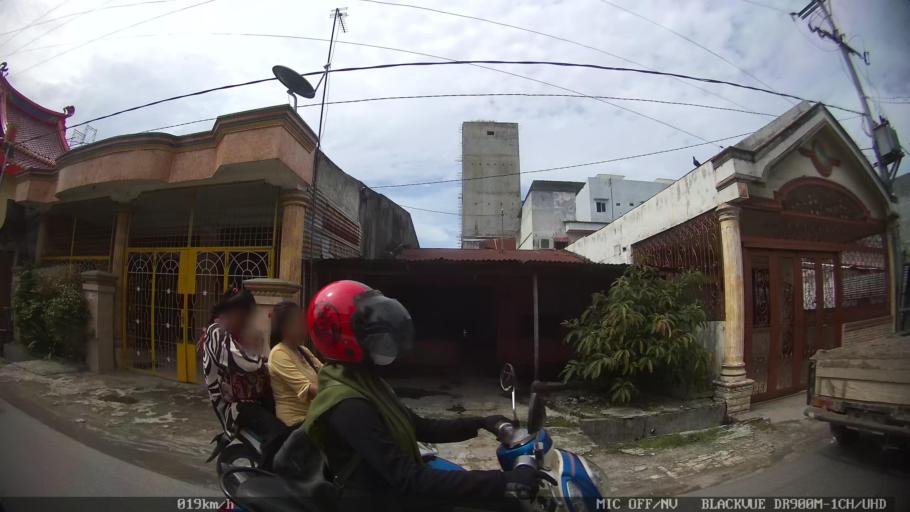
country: ID
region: North Sumatra
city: Percut
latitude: 3.6138
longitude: 98.8020
